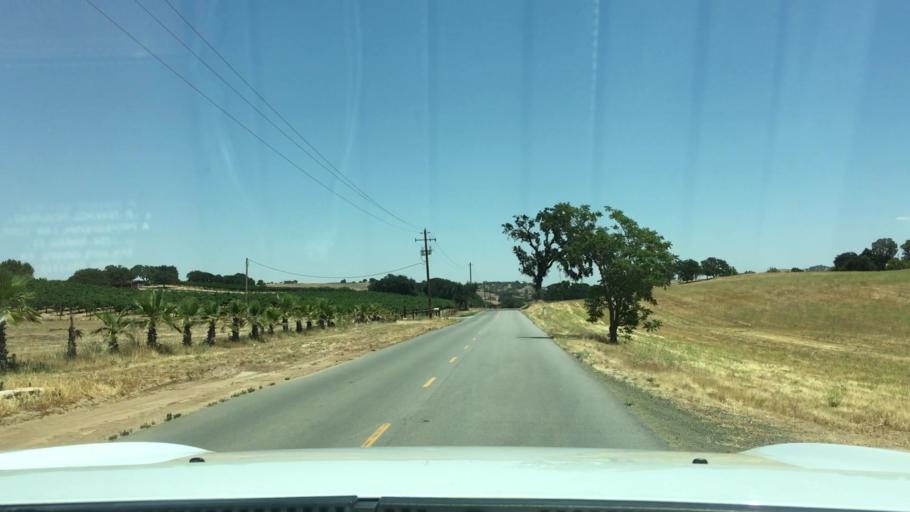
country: US
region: California
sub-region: San Luis Obispo County
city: Paso Robles
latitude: 35.6104
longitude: -120.6181
